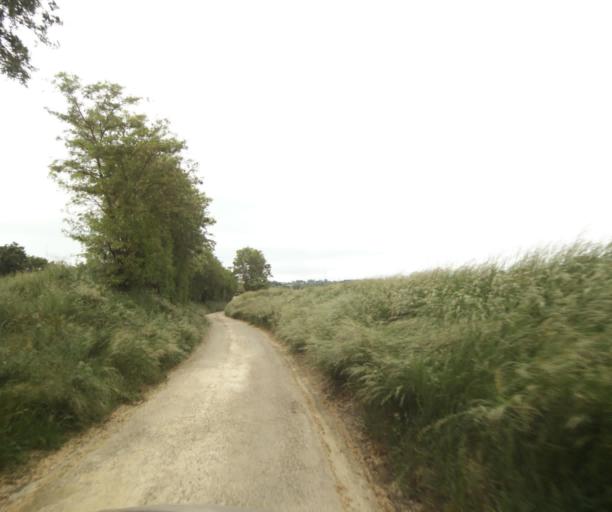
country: FR
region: Rhone-Alpes
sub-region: Departement de l'Ain
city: Miribel
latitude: 45.8488
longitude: 4.9448
